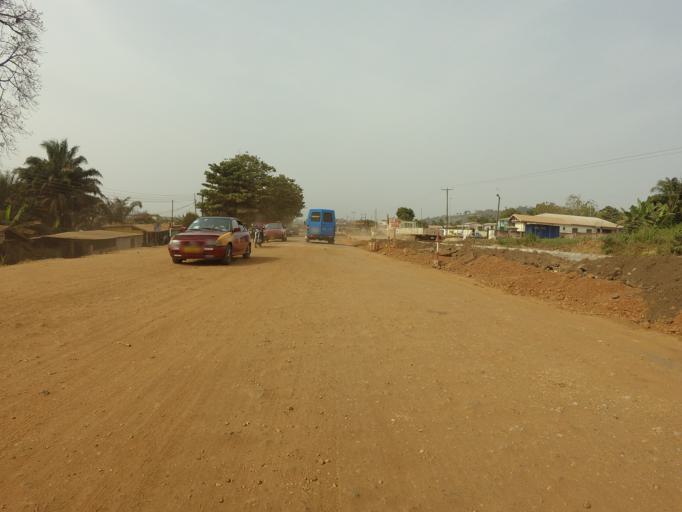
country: GH
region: Volta
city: Ho
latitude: 6.5990
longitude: 0.4478
